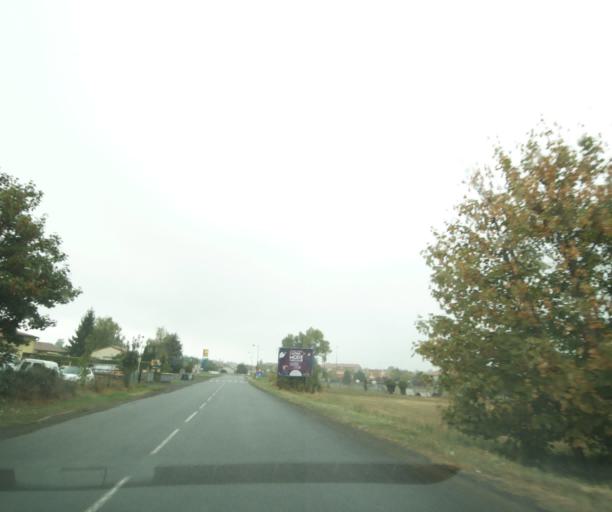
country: FR
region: Auvergne
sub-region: Departement du Puy-de-Dome
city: Chateaugay
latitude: 45.8481
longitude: 3.0831
